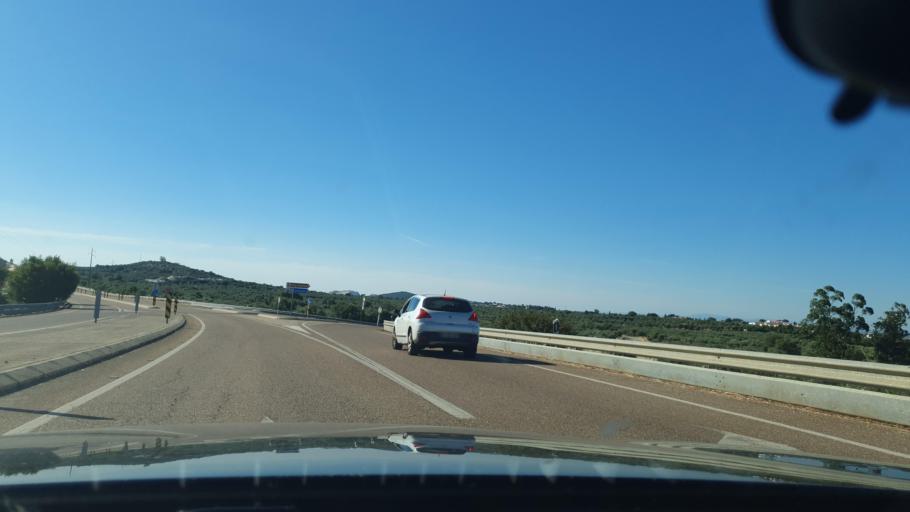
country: PT
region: Evora
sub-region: Vila Vicosa
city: Vila Vicosa
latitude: 38.7554
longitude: -7.4101
